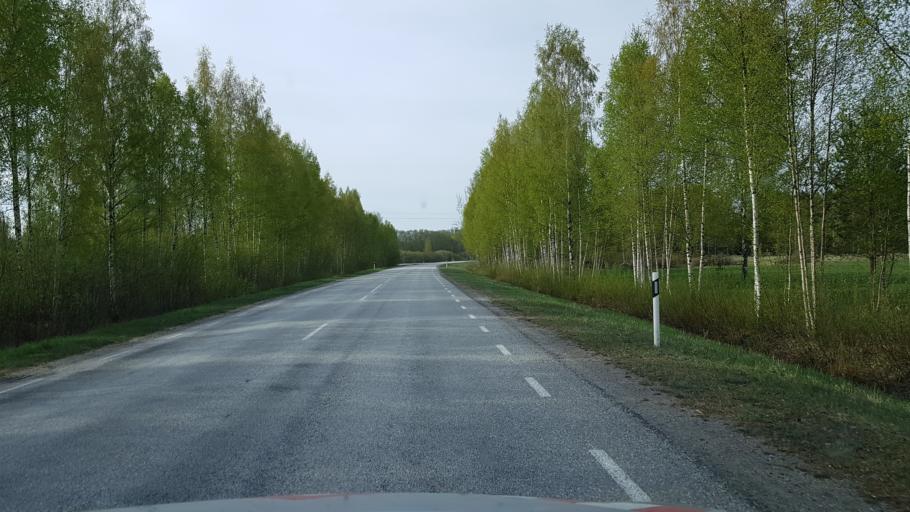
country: EE
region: Paernumaa
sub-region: Audru vald
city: Audru
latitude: 58.4081
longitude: 24.3075
